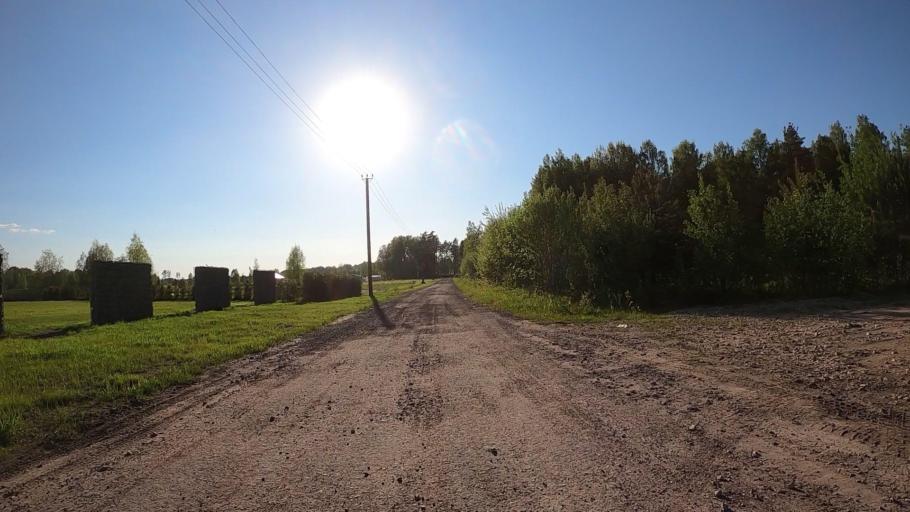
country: LV
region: Baldone
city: Baldone
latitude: 56.7744
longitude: 24.3142
